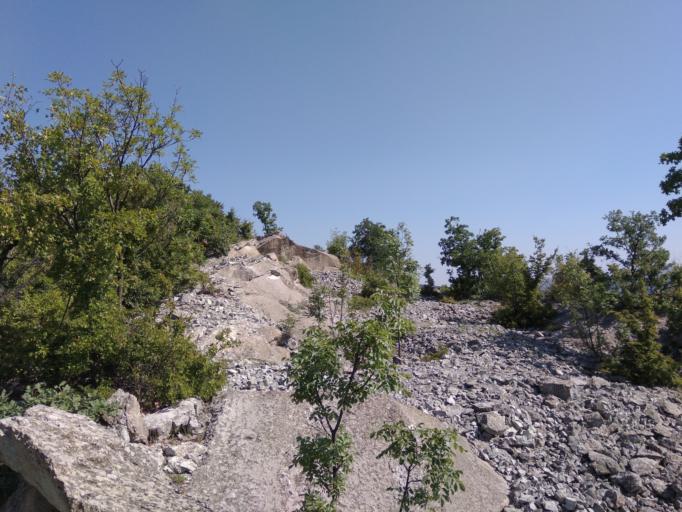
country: BG
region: Kurdzhali
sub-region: Obshtina Krumovgrad
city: Krumovgrad
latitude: 41.5145
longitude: 25.6647
